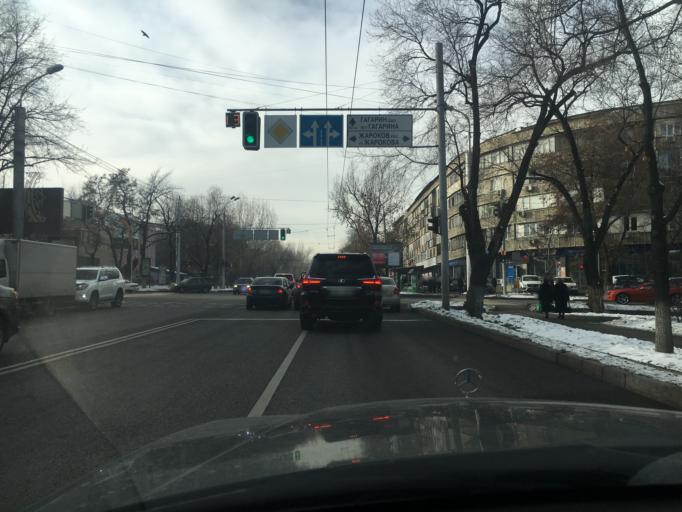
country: KZ
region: Almaty Qalasy
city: Almaty
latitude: 43.2324
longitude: 76.9009
